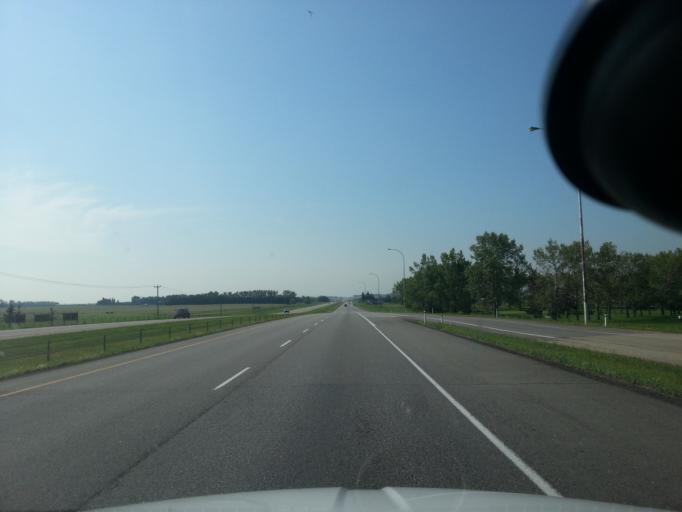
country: CA
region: Alberta
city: Olds
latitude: 51.9298
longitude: -114.0255
